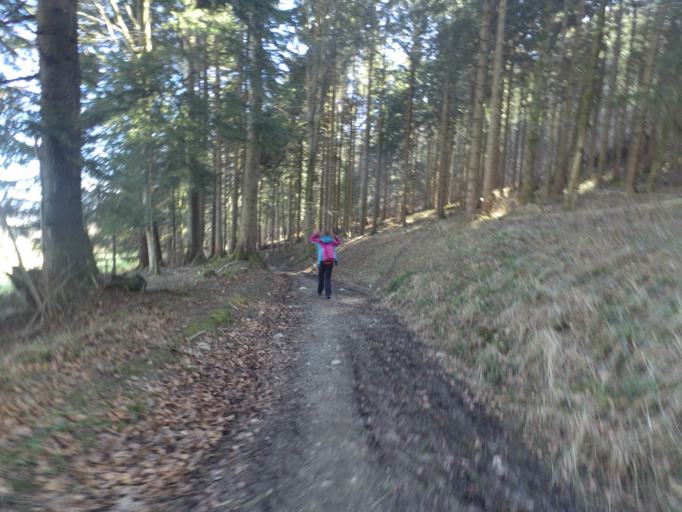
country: AT
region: Salzburg
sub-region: Politischer Bezirk Salzburg-Umgebung
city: Koppl
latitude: 47.8025
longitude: 13.1356
